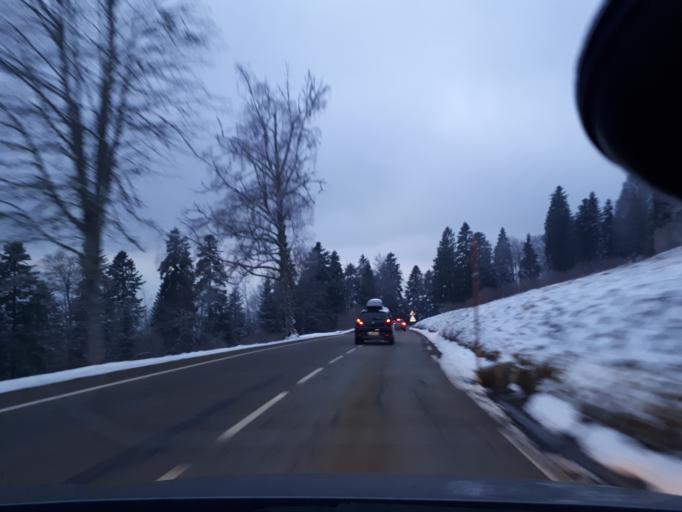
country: FR
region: Rhone-Alpes
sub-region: Departement de l'Isere
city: Vaulnaveys-le-Bas
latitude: 45.1024
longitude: 5.8438
